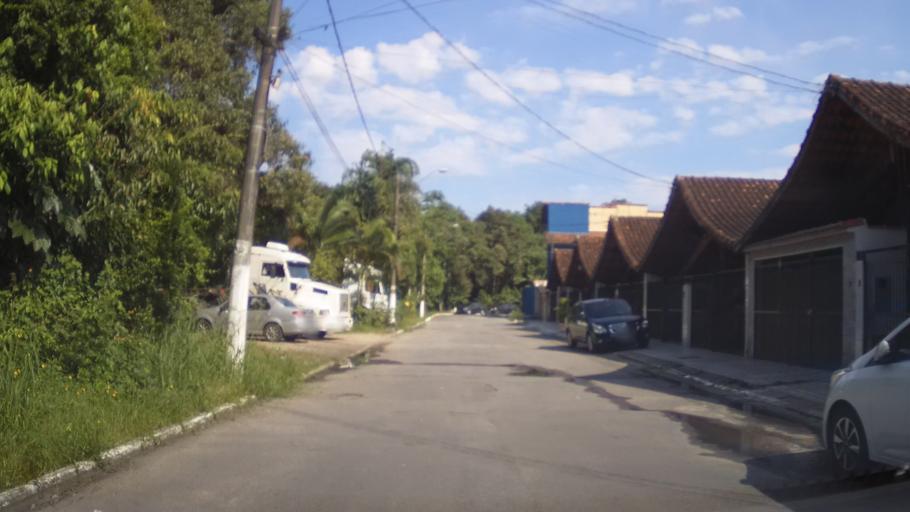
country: BR
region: Sao Paulo
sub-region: Praia Grande
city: Praia Grande
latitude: -23.9917
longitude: -46.4138
